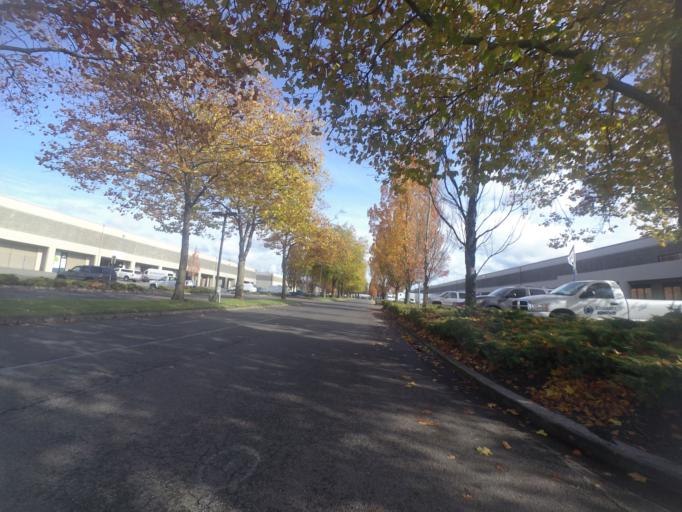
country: US
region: Washington
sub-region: Pierce County
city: Lakewood
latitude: 47.1710
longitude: -122.4974
